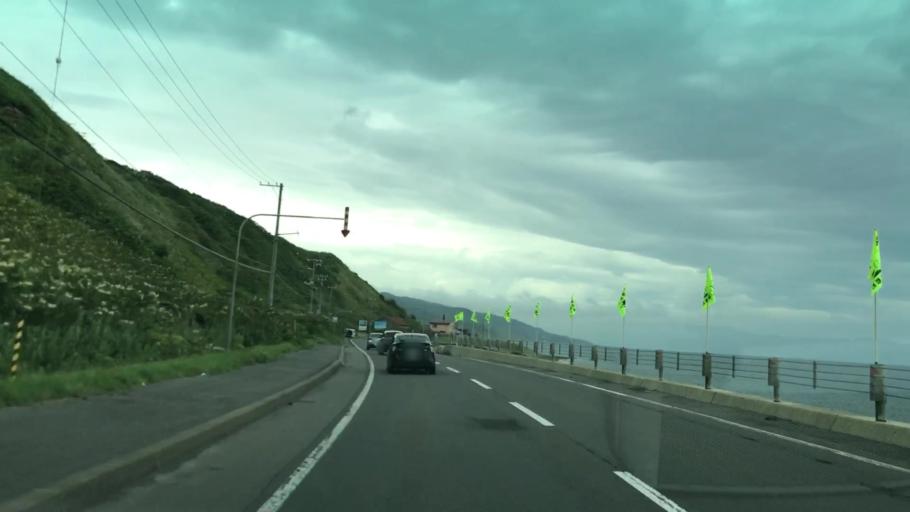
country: JP
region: Hokkaido
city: Iwanai
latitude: 42.8723
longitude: 140.3583
